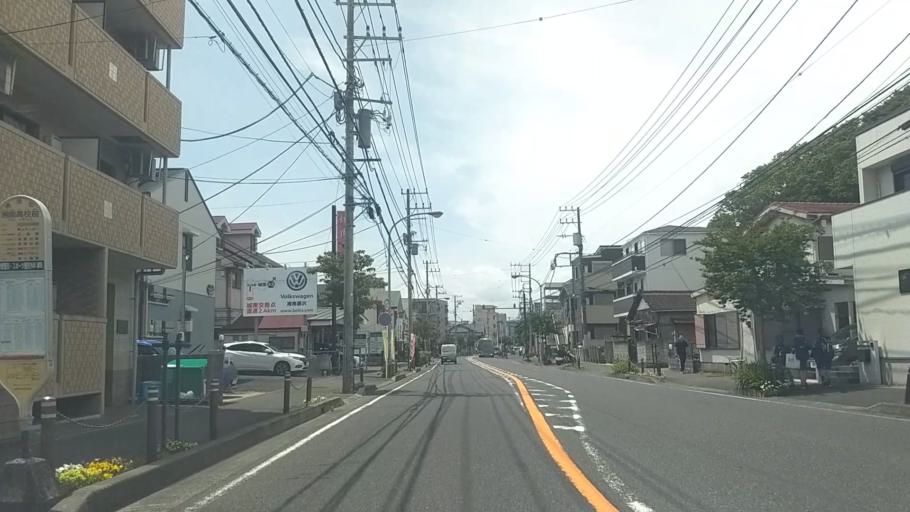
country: JP
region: Kanagawa
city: Fujisawa
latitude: 35.3466
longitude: 139.4722
